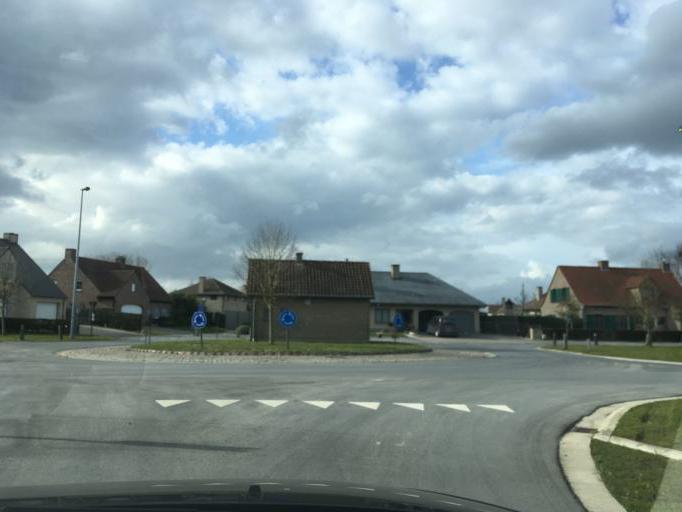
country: BE
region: Flanders
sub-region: Provincie West-Vlaanderen
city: Roeselare
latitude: 50.9244
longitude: 3.1499
